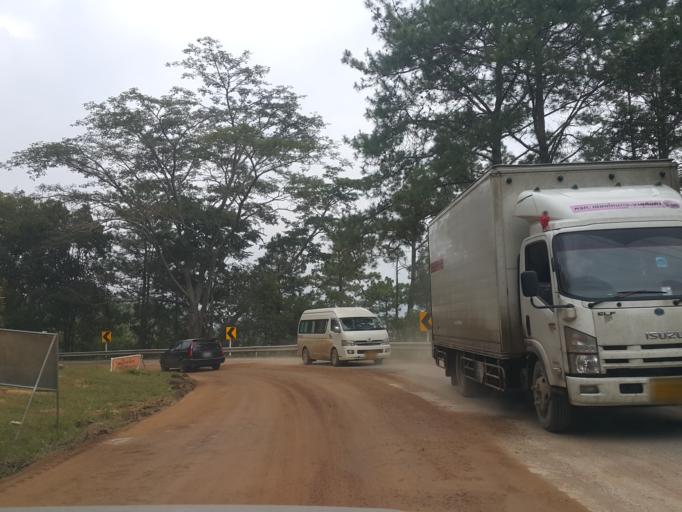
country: TH
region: Mae Hong Son
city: Mae Hi
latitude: 19.2728
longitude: 98.5539
